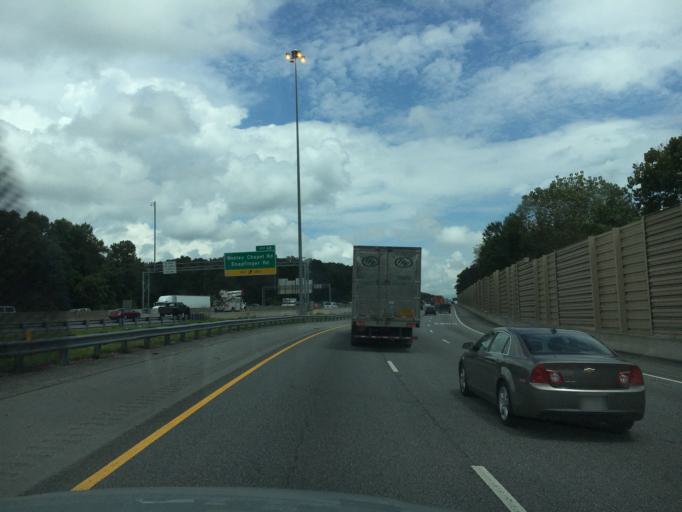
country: US
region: Georgia
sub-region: DeKalb County
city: Panthersville
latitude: 33.7140
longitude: -84.2384
